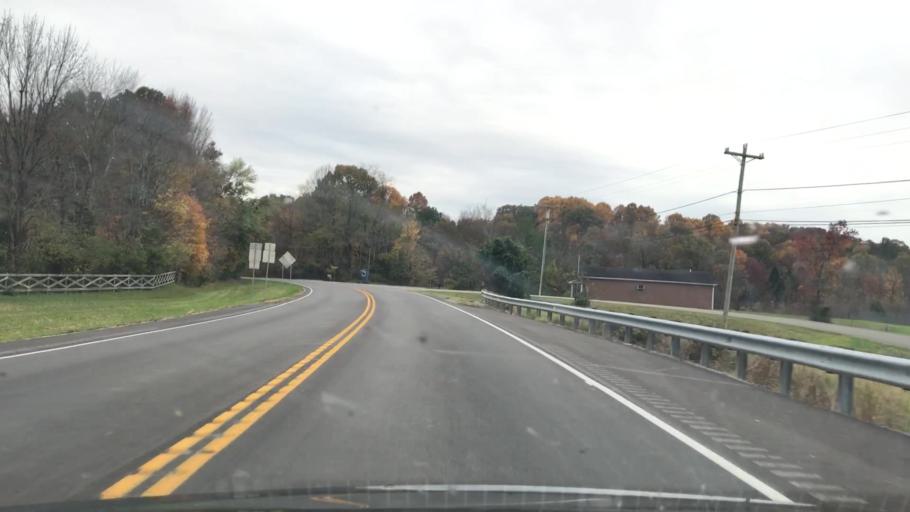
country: US
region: Kentucky
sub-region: Barren County
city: Glasgow
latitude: 37.0313
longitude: -85.9075
